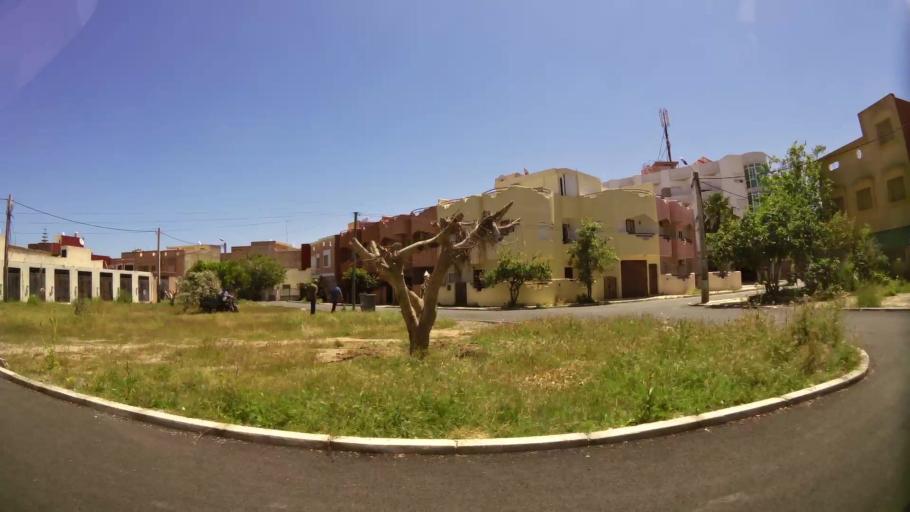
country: MA
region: Oriental
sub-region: Berkane-Taourirt
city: Madagh
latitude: 35.0820
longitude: -2.2343
